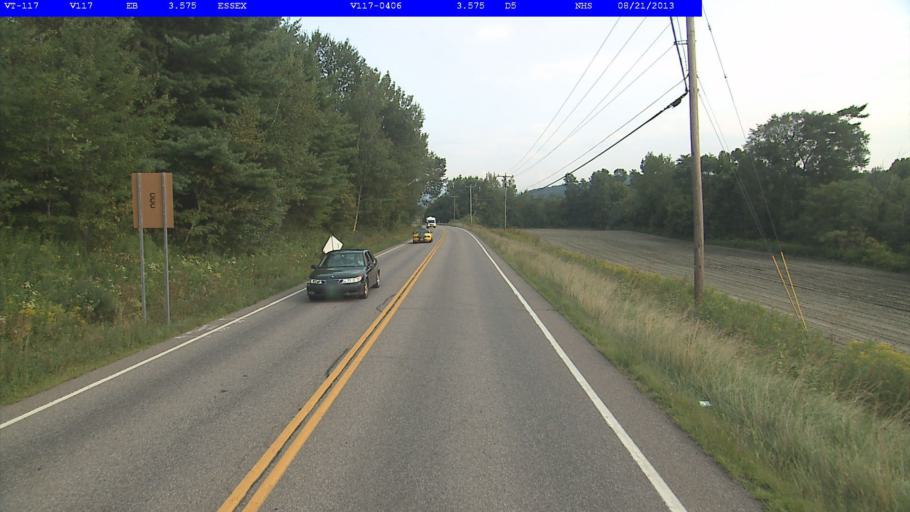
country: US
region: Vermont
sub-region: Chittenden County
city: Williston
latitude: 44.4778
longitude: -73.0440
